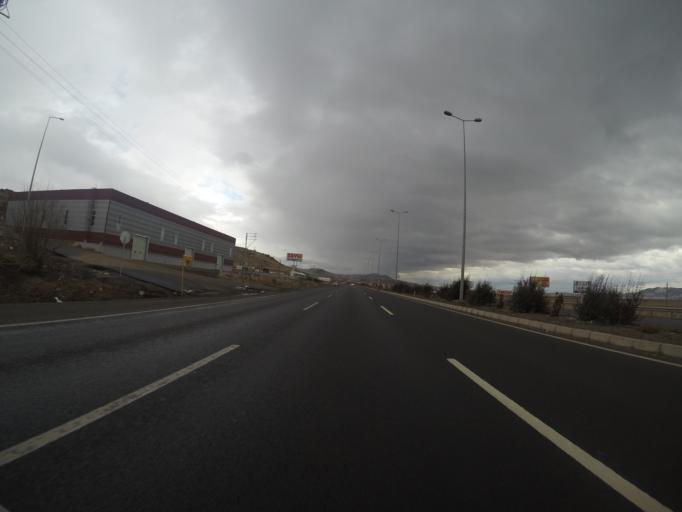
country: TR
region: Kayseri
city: Melikgazi
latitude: 38.7425
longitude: 35.2972
